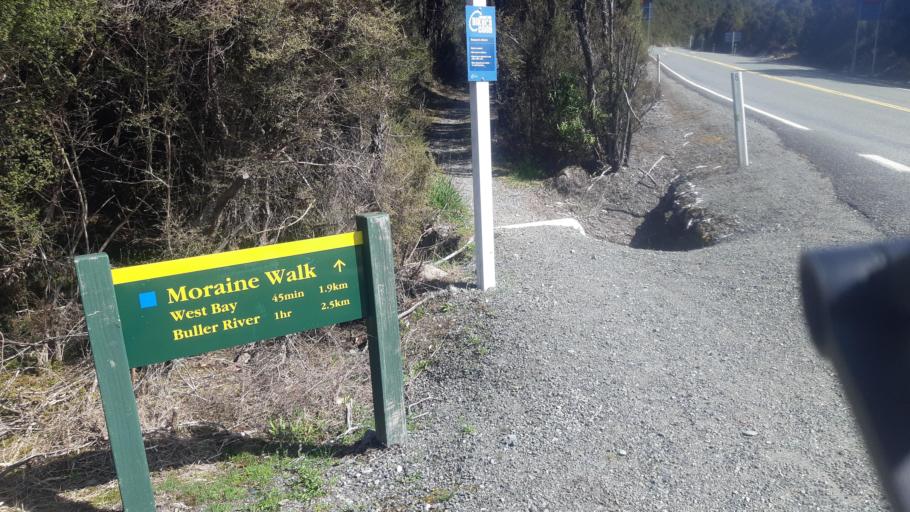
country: NZ
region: Tasman
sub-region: Tasman District
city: Wakefield
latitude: -41.8015
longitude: 172.8402
